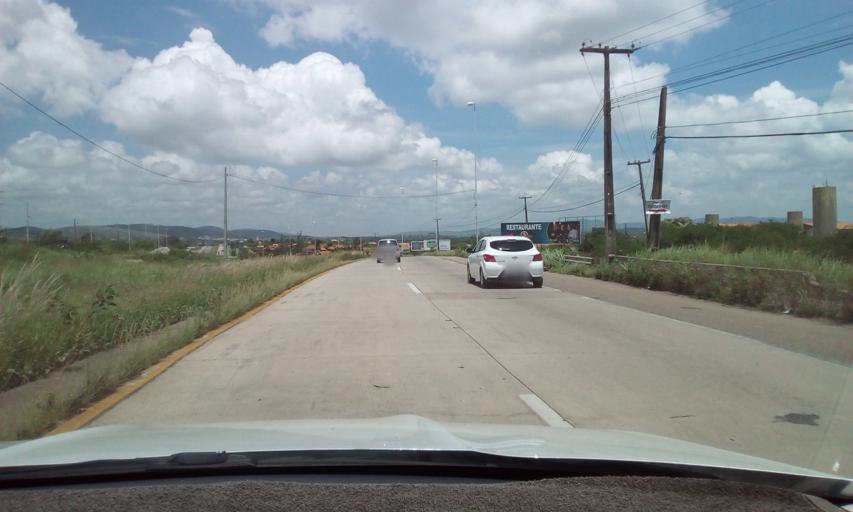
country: BR
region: Pernambuco
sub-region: Gravata
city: Gravata
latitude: -8.2026
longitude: -35.5956
